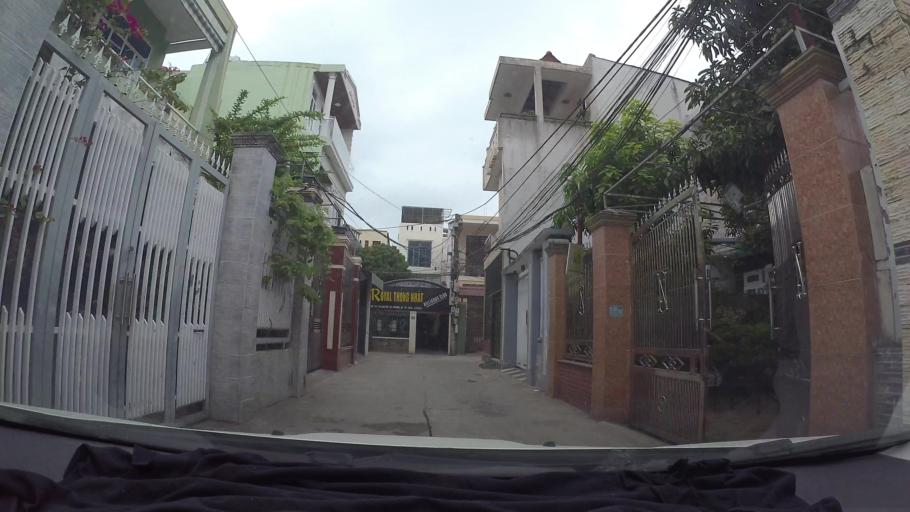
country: VN
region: Da Nang
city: Da Nang
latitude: 16.0515
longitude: 108.2130
